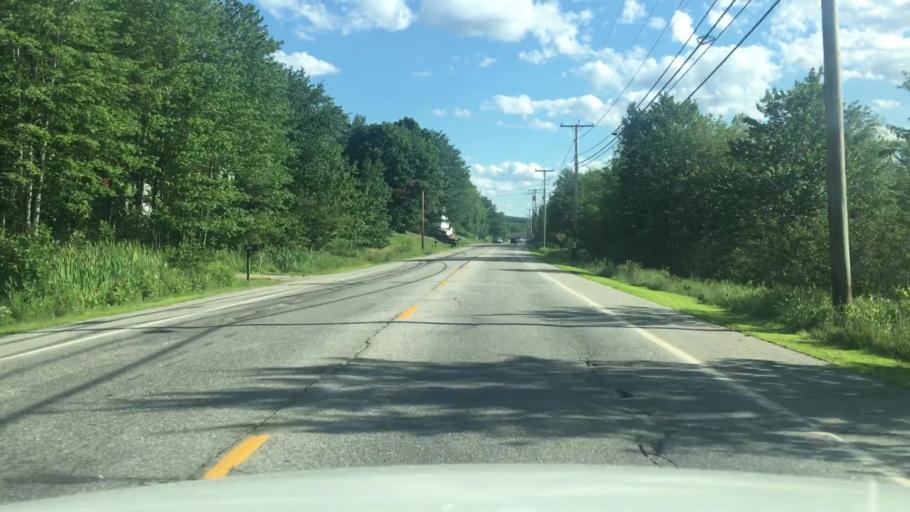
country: US
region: Maine
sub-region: Franklin County
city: Wilton
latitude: 44.5532
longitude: -70.2367
